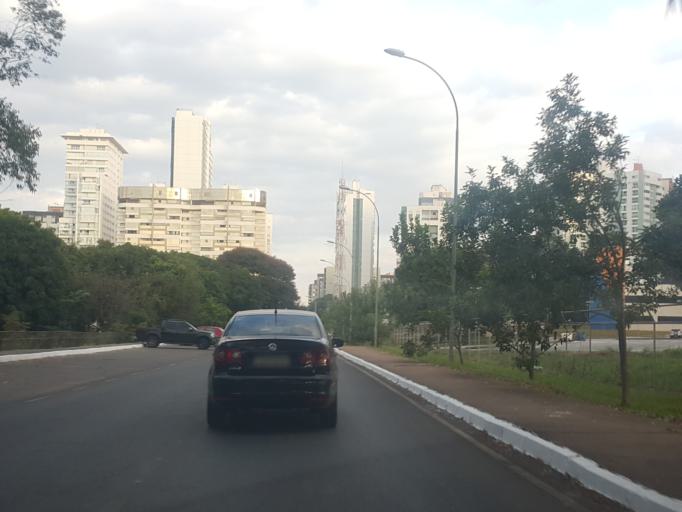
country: BR
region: Federal District
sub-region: Brasilia
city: Brasilia
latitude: -15.8353
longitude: -48.0259
